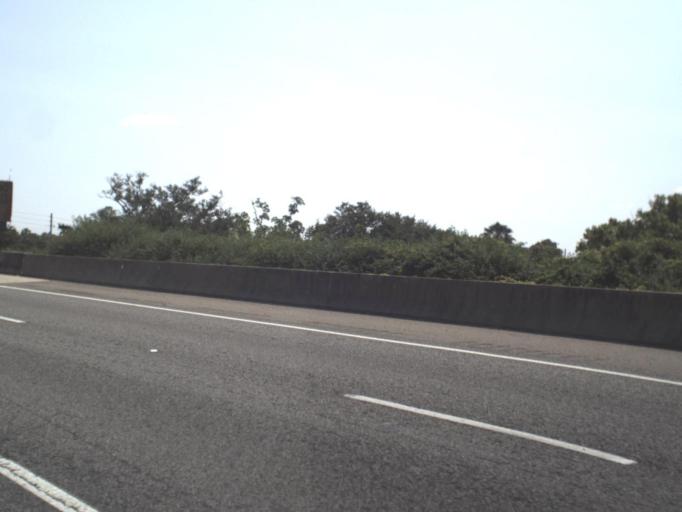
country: US
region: Florida
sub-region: Duval County
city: Jacksonville
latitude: 30.3333
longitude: -81.6711
